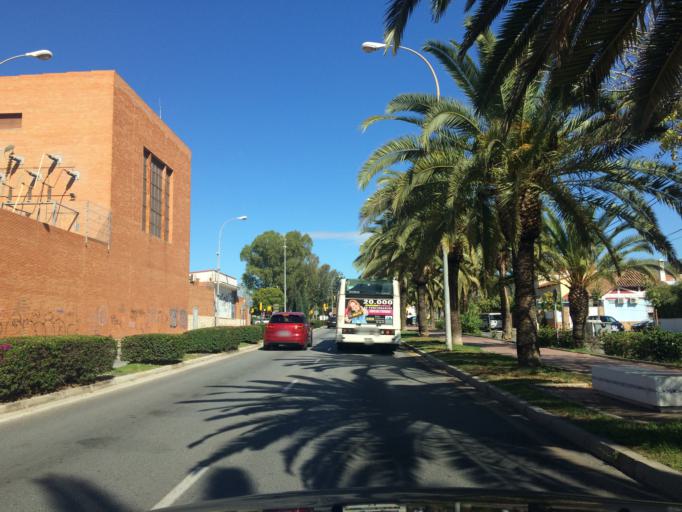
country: ES
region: Andalusia
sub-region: Provincia de Malaga
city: Malaga
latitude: 36.7365
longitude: -4.4247
